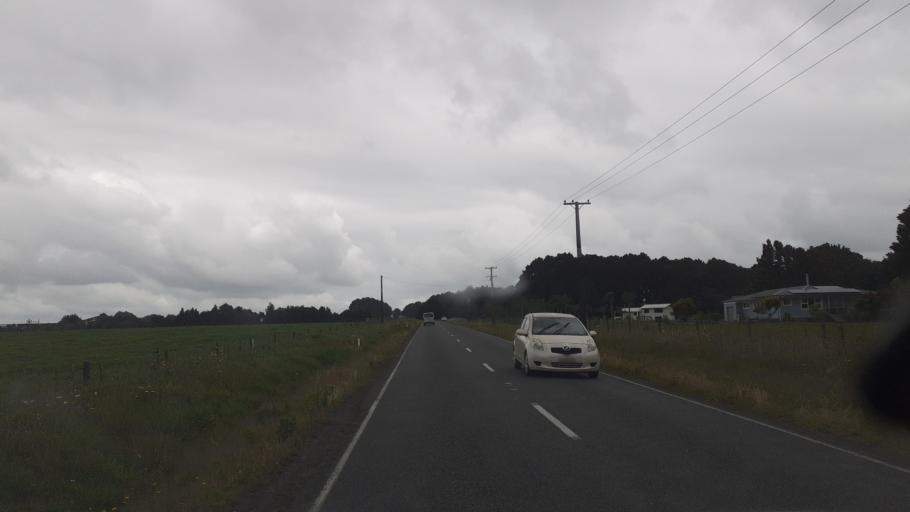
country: NZ
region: Northland
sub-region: Far North District
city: Waimate North
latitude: -35.2884
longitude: 173.8264
